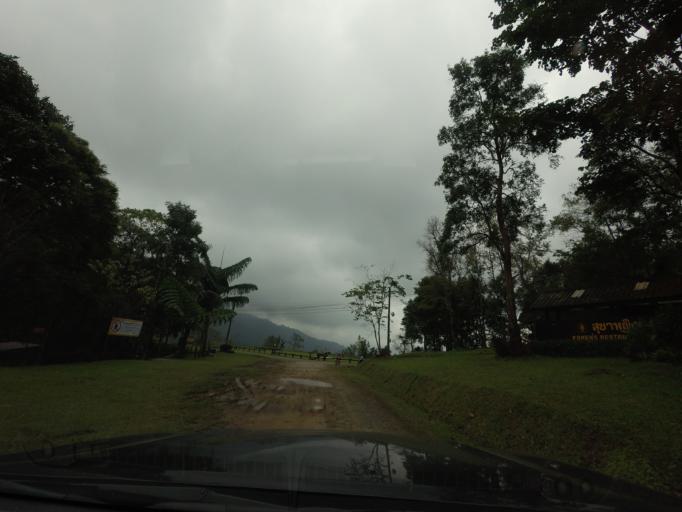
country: TH
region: Nan
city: Bo Kluea
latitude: 19.2045
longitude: 101.0808
